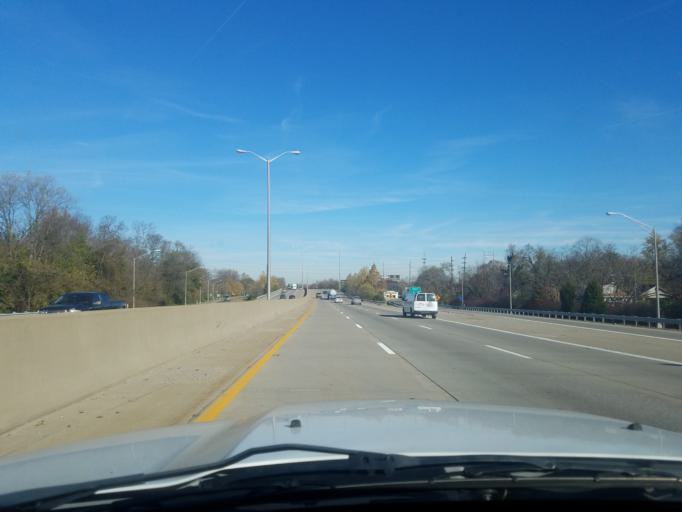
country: US
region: Indiana
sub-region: Floyd County
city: New Albany
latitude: 38.2512
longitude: -85.8066
